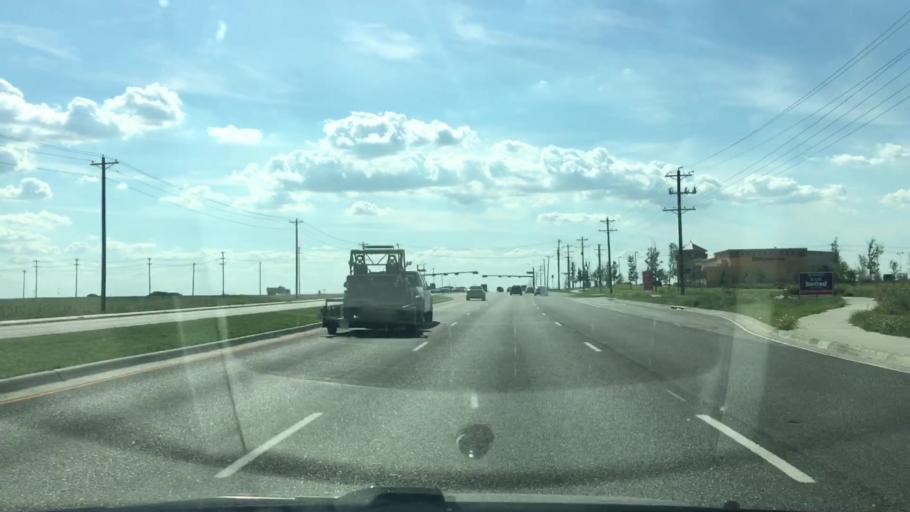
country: US
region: Texas
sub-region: Collin County
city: Prosper
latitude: 33.2188
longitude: -96.7643
